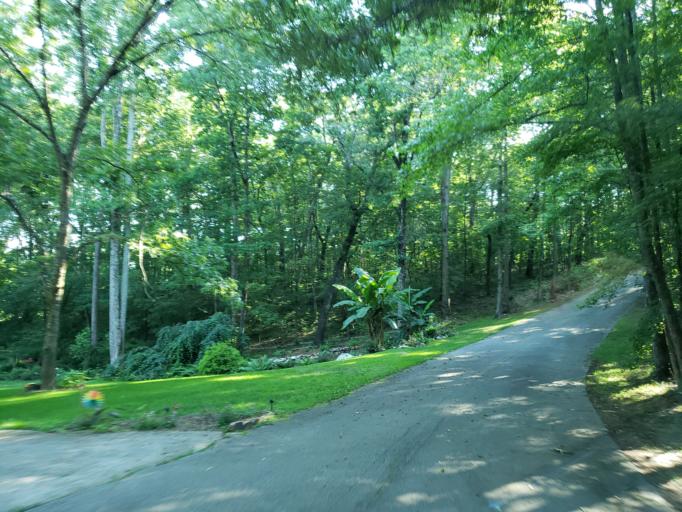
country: US
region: Georgia
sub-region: Haralson County
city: Bremen
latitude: 33.7586
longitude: -85.1589
